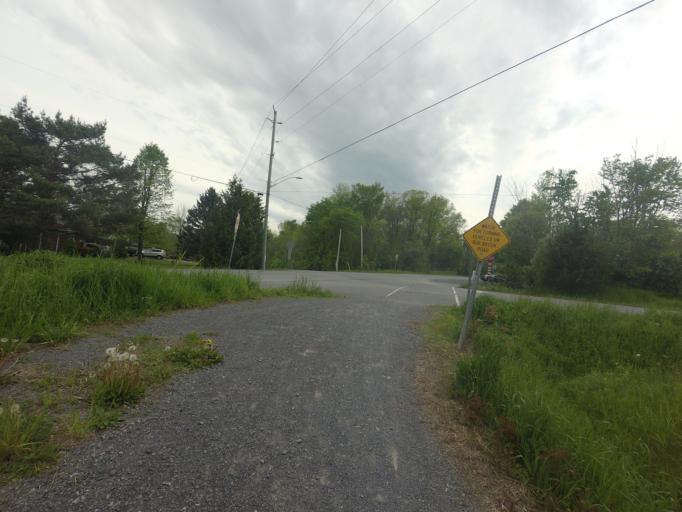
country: CA
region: Ontario
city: Kingston
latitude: 44.2984
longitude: -76.5746
